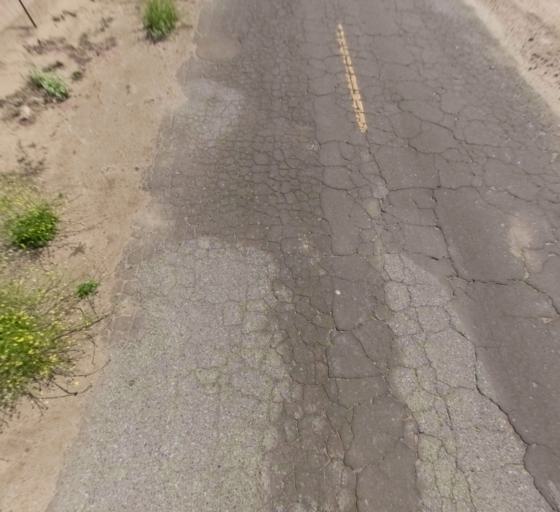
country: US
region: California
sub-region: Madera County
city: Parkwood
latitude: 36.9275
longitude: -120.0306
